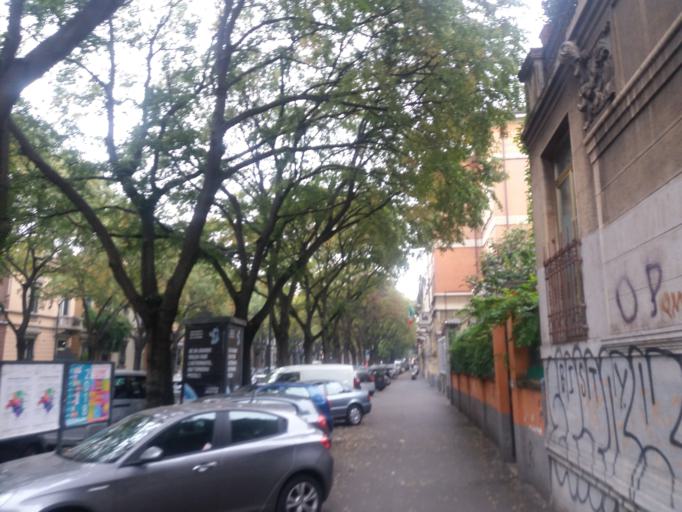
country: IT
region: Lombardy
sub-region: Citta metropolitana di Milano
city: Milano
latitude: 45.4843
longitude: 9.2237
